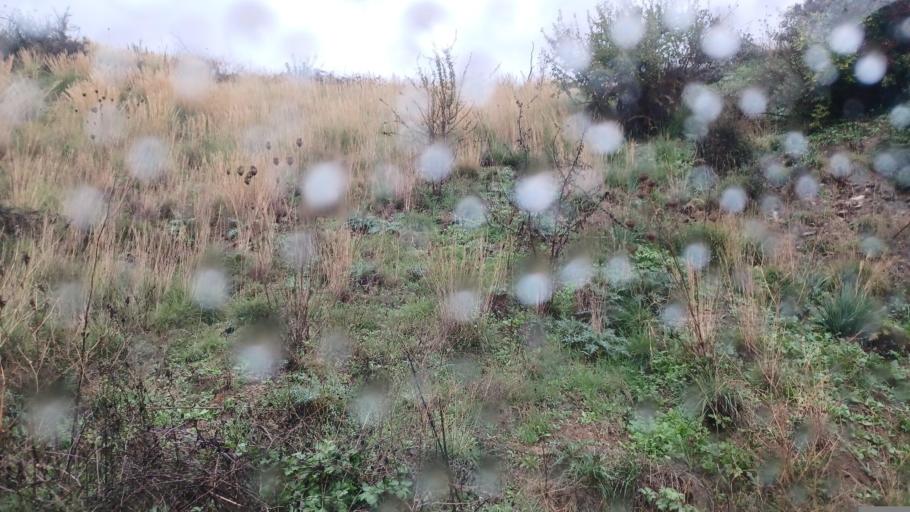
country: CY
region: Pafos
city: Mesogi
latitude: 34.8644
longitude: 32.5445
